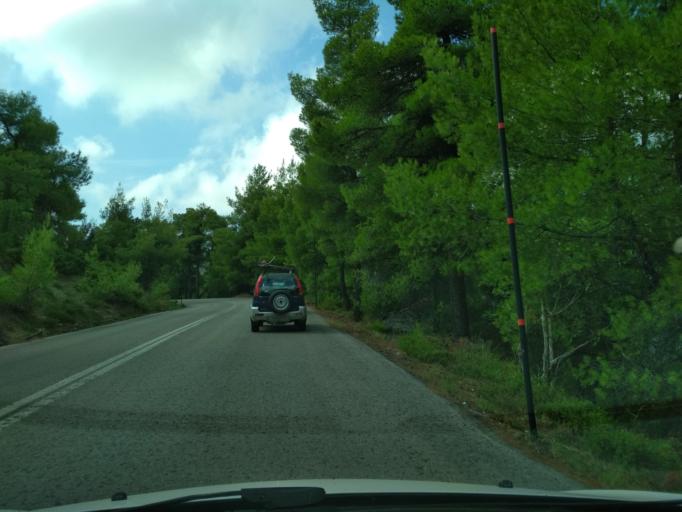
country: GR
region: Central Greece
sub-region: Nomos Evvoias
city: Politika
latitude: 38.6726
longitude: 23.5572
